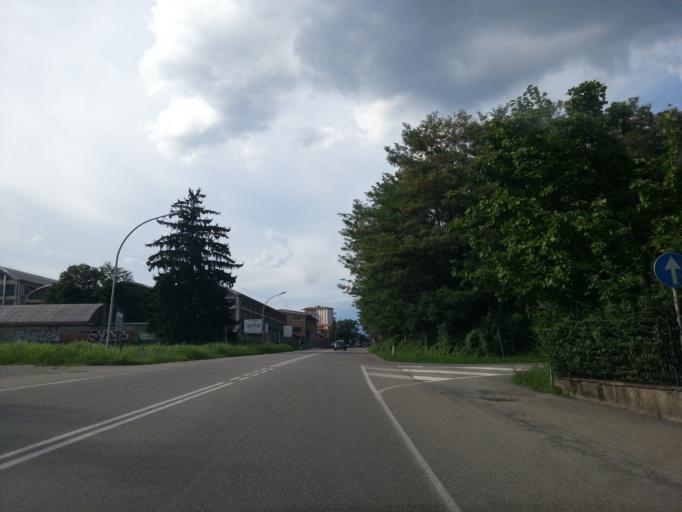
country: IT
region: Lombardy
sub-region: Provincia di Monza e Brianza
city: Carate Brianza
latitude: 45.6684
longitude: 9.2451
